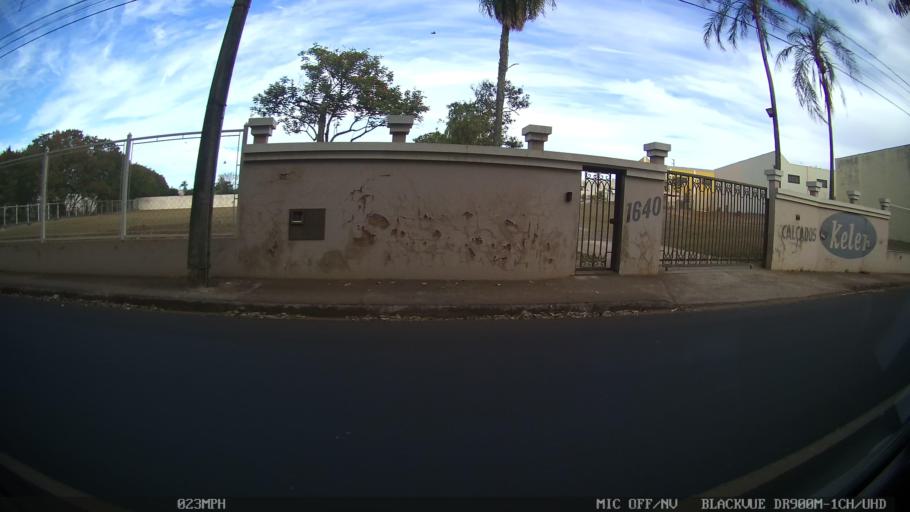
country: BR
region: Sao Paulo
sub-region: Catanduva
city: Catanduva
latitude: -21.1222
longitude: -48.9910
